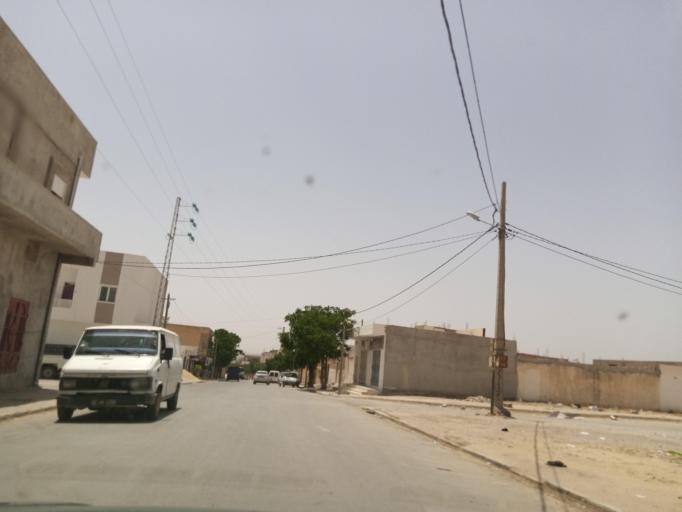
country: TN
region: Al Qasrayn
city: Kasserine
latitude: 35.2112
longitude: 8.8942
